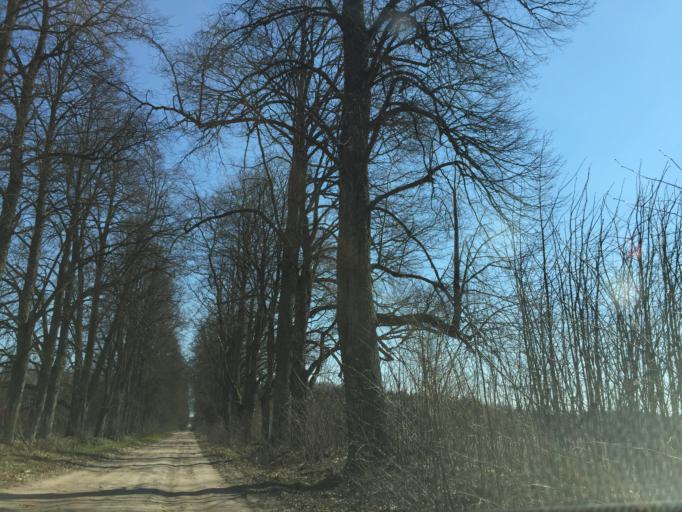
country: EE
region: Tartu
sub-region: Tartu linn
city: Tartu
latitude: 58.5281
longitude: 26.8847
